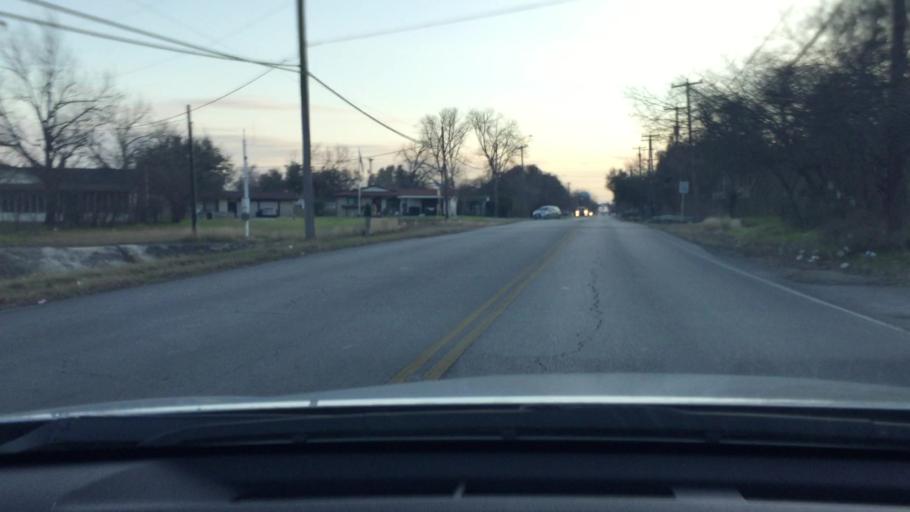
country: US
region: Texas
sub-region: Bexar County
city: Terrell Hills
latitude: 29.4953
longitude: -98.4246
